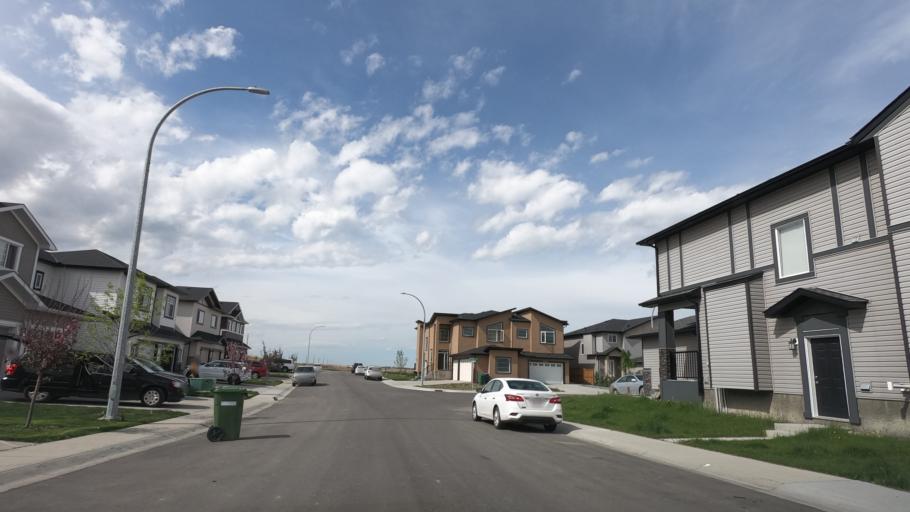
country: CA
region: Alberta
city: Airdrie
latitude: 51.2758
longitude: -114.0476
